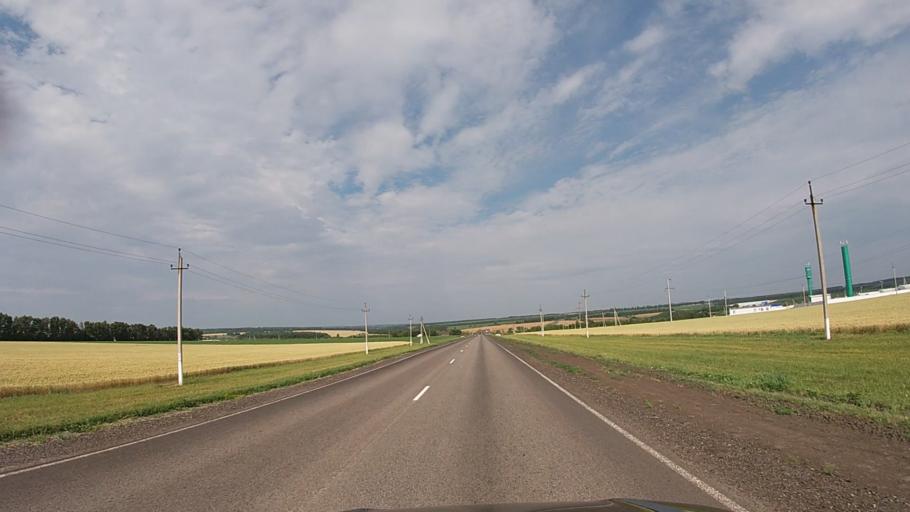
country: RU
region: Belgorod
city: Krasnaya Yaruga
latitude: 50.7981
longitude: 35.5856
